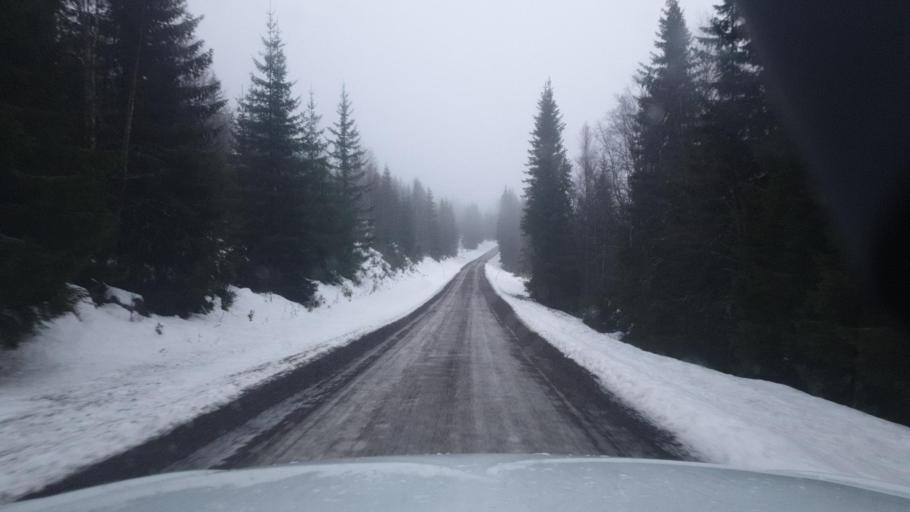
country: SE
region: Vaermland
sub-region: Eda Kommun
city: Charlottenberg
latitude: 60.1021
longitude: 12.6081
